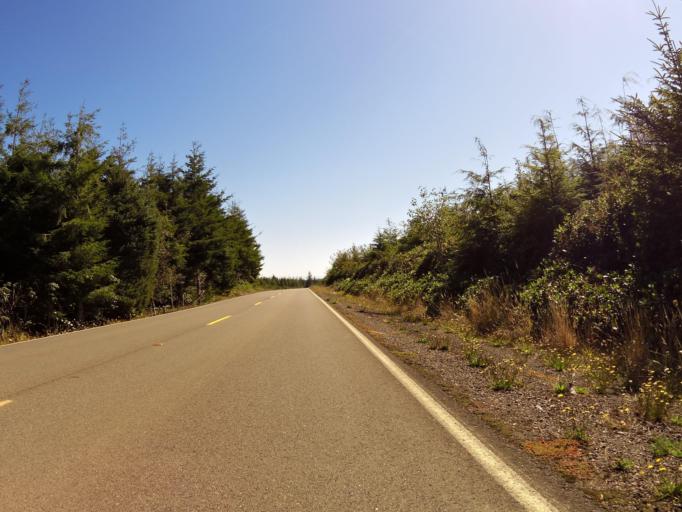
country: US
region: Oregon
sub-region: Coos County
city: Barview
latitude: 43.2599
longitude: -124.3402
